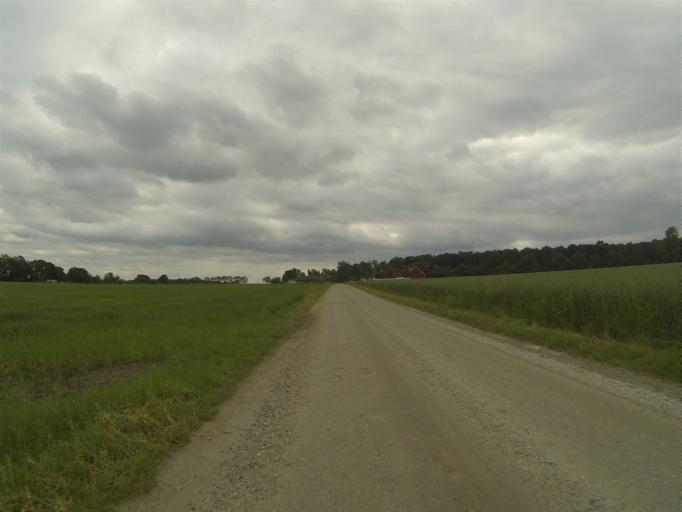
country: SE
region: Skane
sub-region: Lunds Kommun
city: Lund
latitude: 55.7250
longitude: 13.2887
